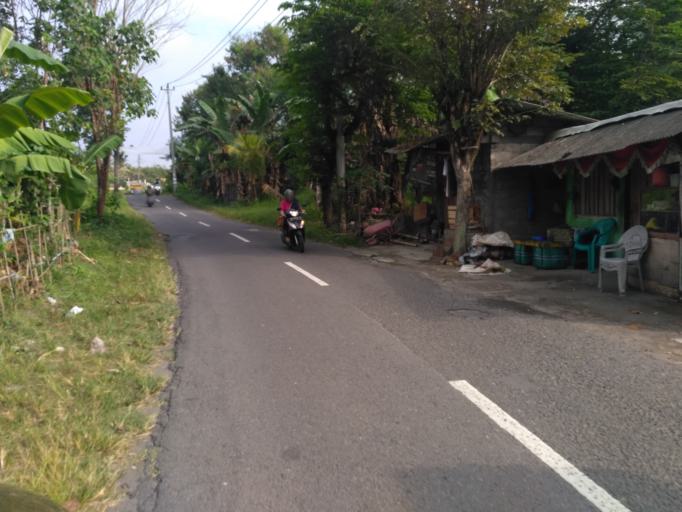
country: ID
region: Daerah Istimewa Yogyakarta
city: Melati
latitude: -7.7139
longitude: 110.3982
